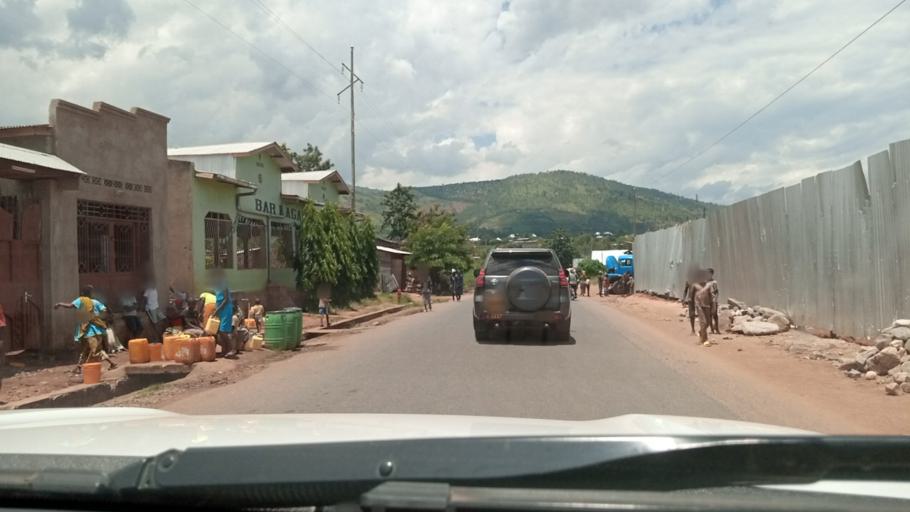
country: BI
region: Bujumbura Mairie
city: Bujumbura
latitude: -3.4771
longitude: 29.3521
